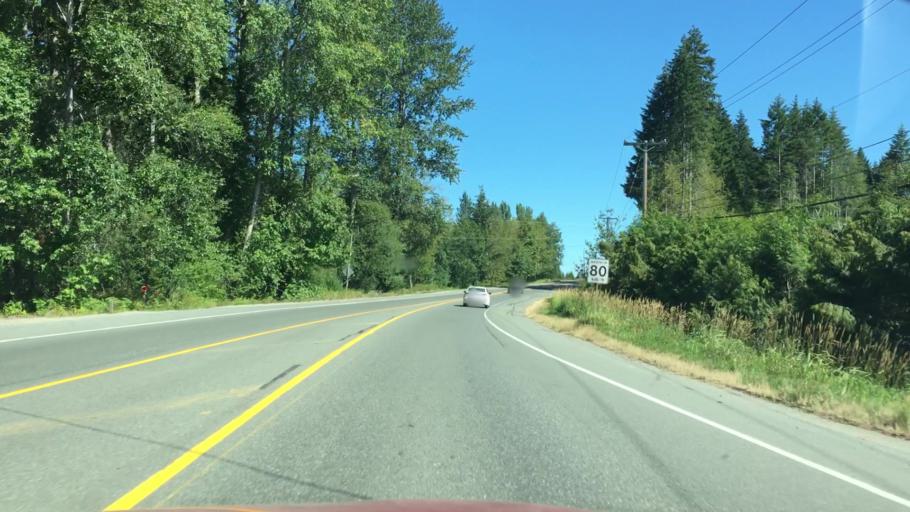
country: CA
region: British Columbia
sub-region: Regional District of Nanaimo
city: Parksville
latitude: 49.3100
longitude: -124.4966
